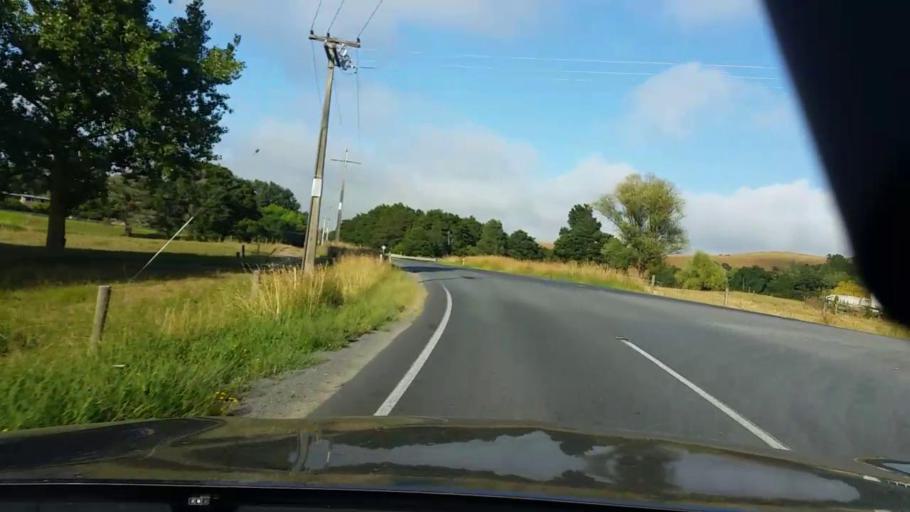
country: NZ
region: Waikato
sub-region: Hamilton City
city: Hamilton
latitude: -37.5938
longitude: 175.3632
